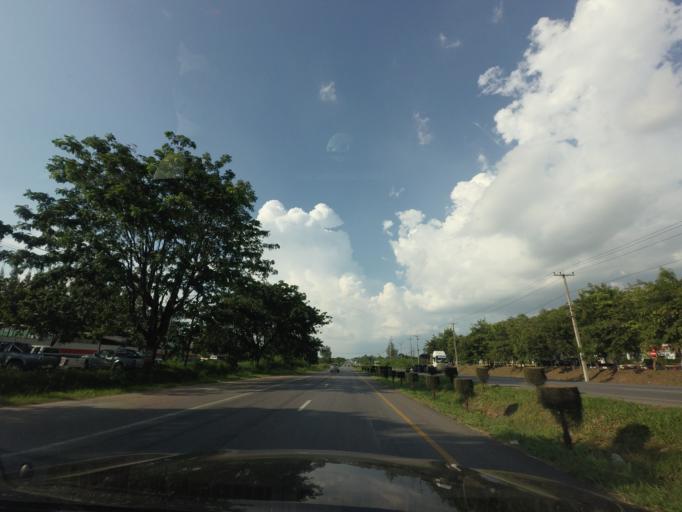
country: TH
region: Khon Kaen
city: Ban Haet
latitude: 16.1756
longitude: 102.7558
